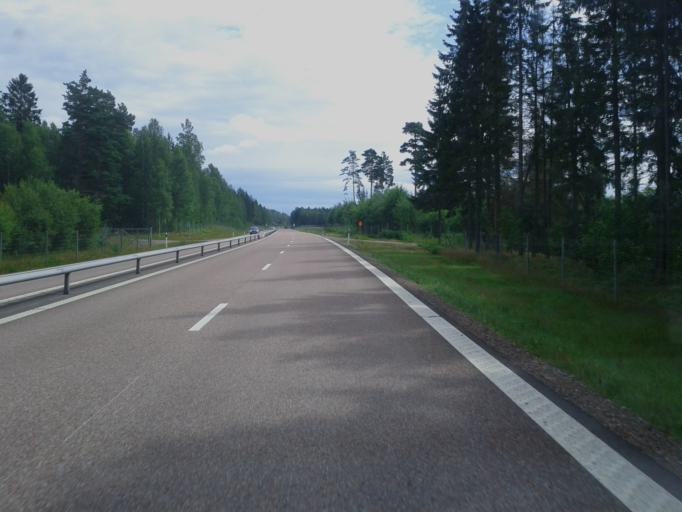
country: SE
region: Dalarna
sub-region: Hedemora Kommun
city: Hedemora
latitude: 60.3225
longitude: 15.8891
